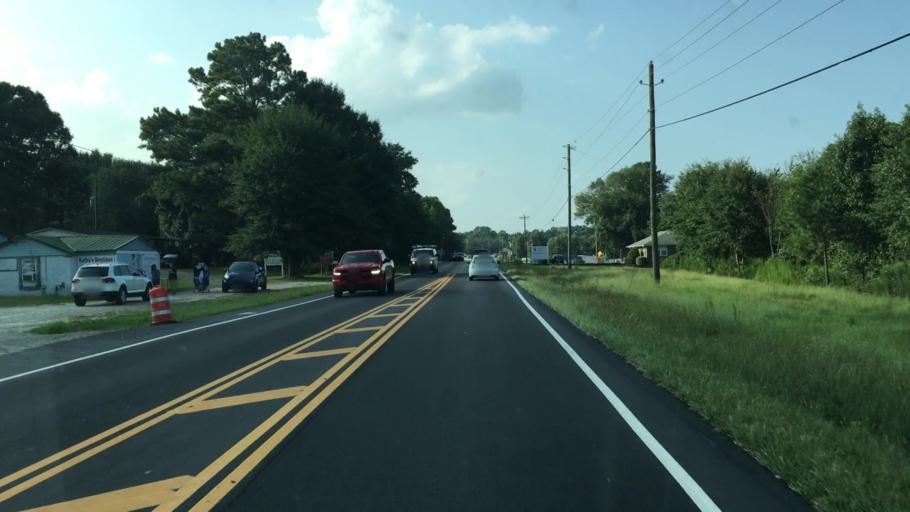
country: US
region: Georgia
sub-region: Jackson County
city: Braselton
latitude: 34.1265
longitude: -83.7650
